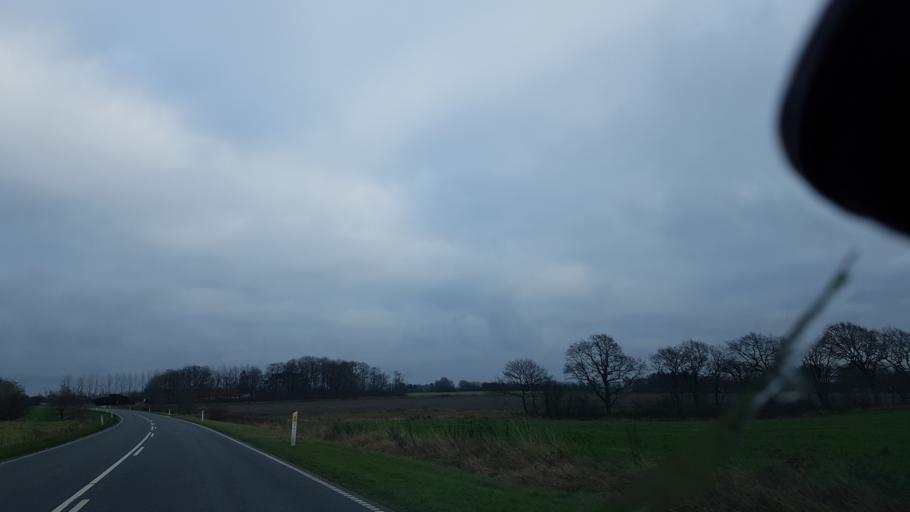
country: DK
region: South Denmark
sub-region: Tonder Kommune
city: Toftlund
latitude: 55.1914
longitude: 9.1017
